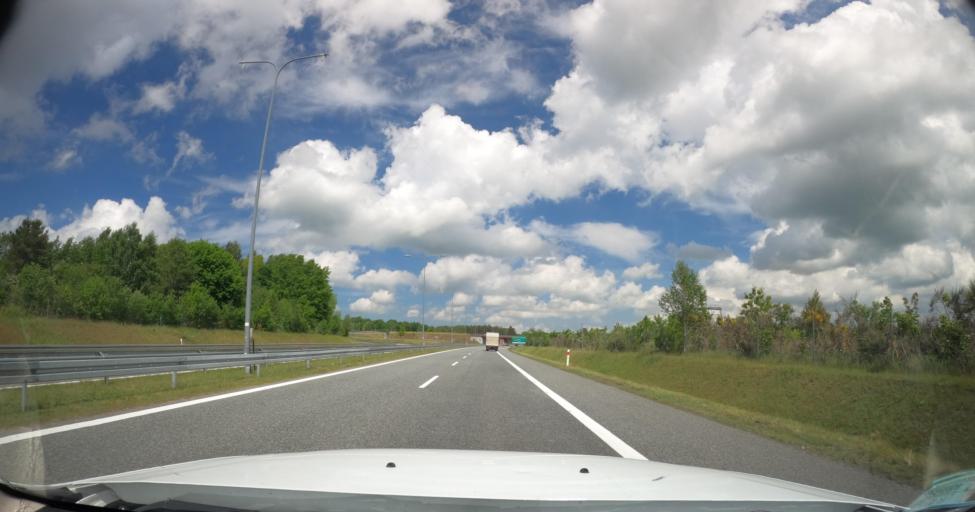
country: PL
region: Pomeranian Voivodeship
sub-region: Slupsk
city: Slupsk
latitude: 54.4483
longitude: 17.0806
